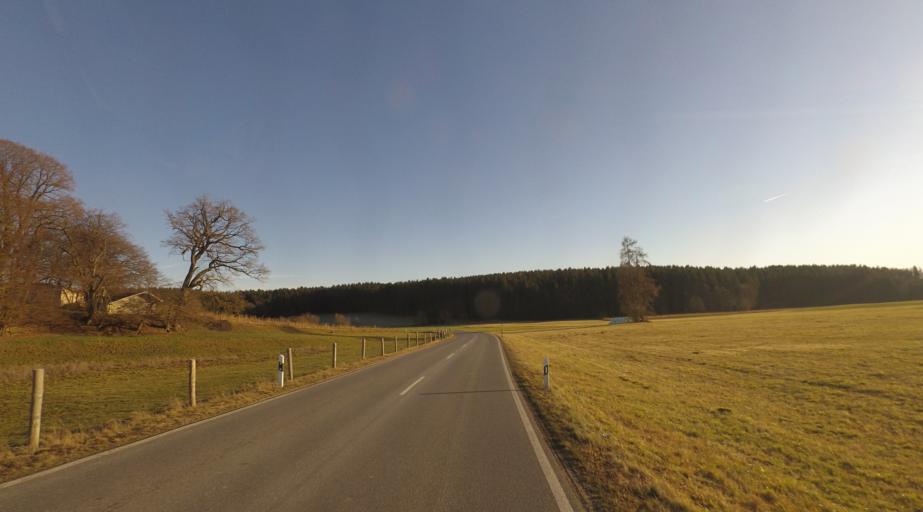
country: DE
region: Bavaria
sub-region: Upper Bavaria
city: Trostberg an der Alz
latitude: 48.0200
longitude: 12.5917
